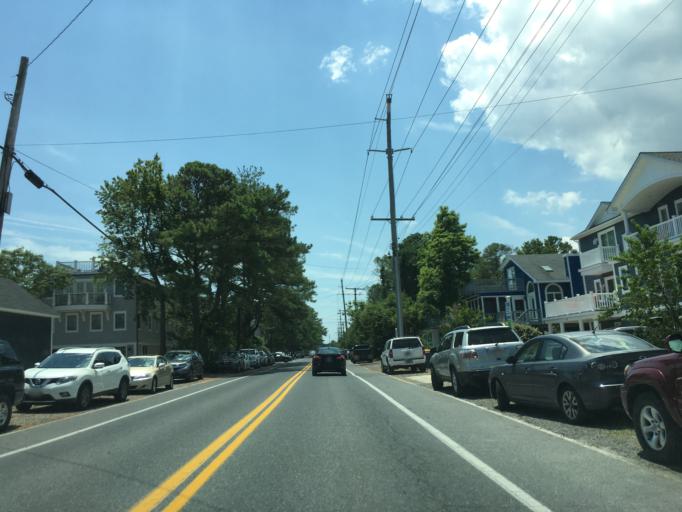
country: US
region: Delaware
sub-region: Sussex County
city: Bethany Beach
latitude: 38.5365
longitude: -75.0571
